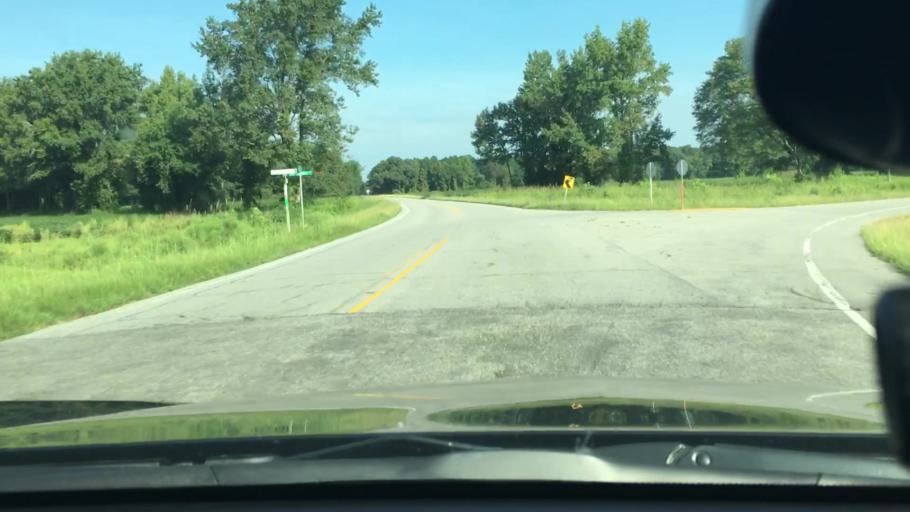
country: US
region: North Carolina
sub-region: Edgecombe County
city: Pinetops
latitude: 35.7534
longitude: -77.5469
